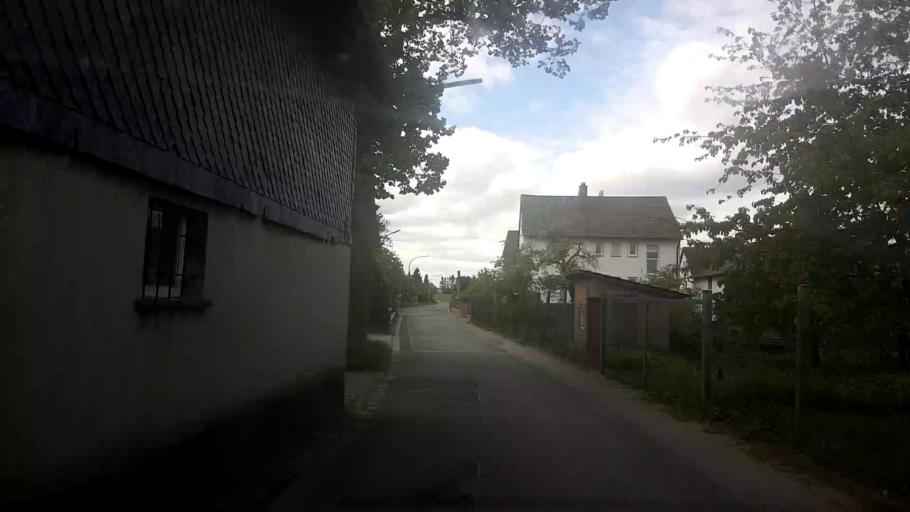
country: DE
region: Bavaria
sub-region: Upper Franconia
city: Lichtenfels
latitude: 50.1218
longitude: 11.0346
